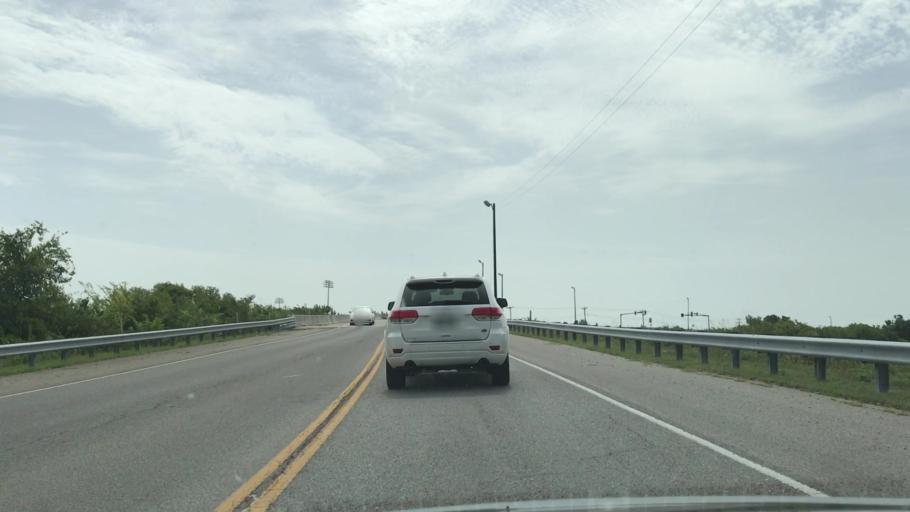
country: US
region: Tennessee
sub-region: Williamson County
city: Brentwood Estates
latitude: 35.9604
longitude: -86.7700
